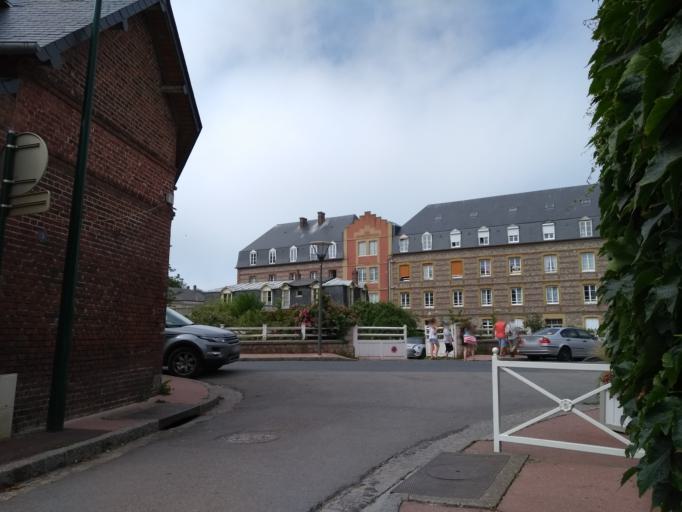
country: FR
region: Haute-Normandie
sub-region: Departement de la Seine-Maritime
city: Saint-Valery-en-Caux
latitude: 49.8757
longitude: 0.7979
